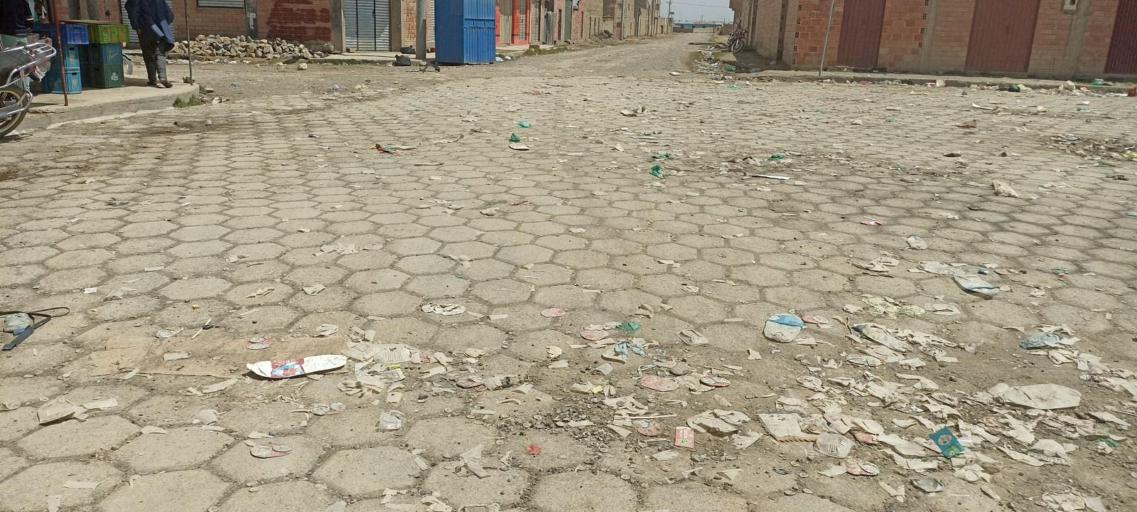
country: BO
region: La Paz
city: Batallas
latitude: -16.4084
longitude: -68.5416
